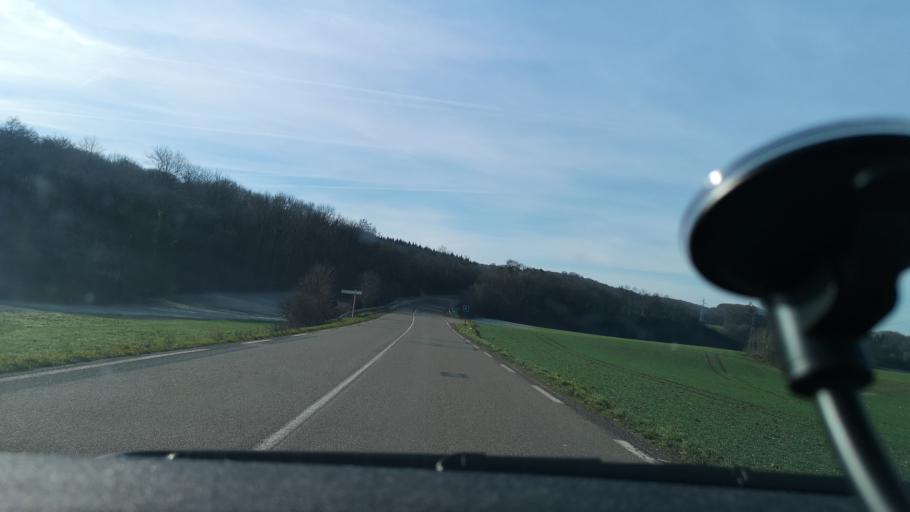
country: FR
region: Franche-Comte
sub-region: Departement du Doubs
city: Roulans
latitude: 47.3320
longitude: 6.2715
